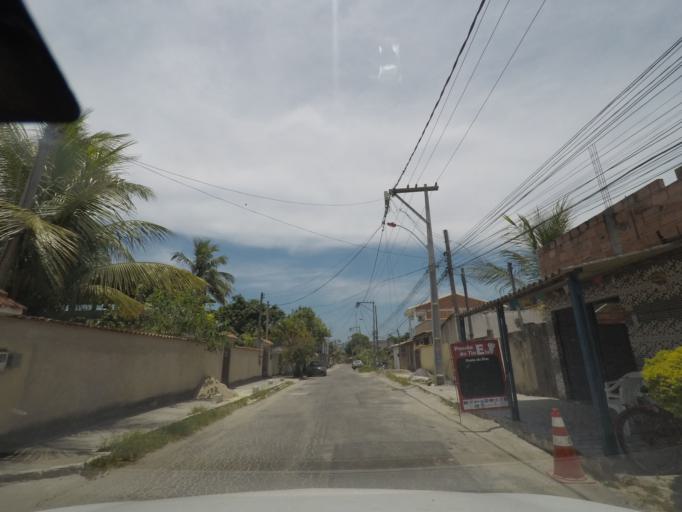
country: BR
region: Rio de Janeiro
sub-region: Marica
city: Marica
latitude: -22.9111
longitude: -42.8407
